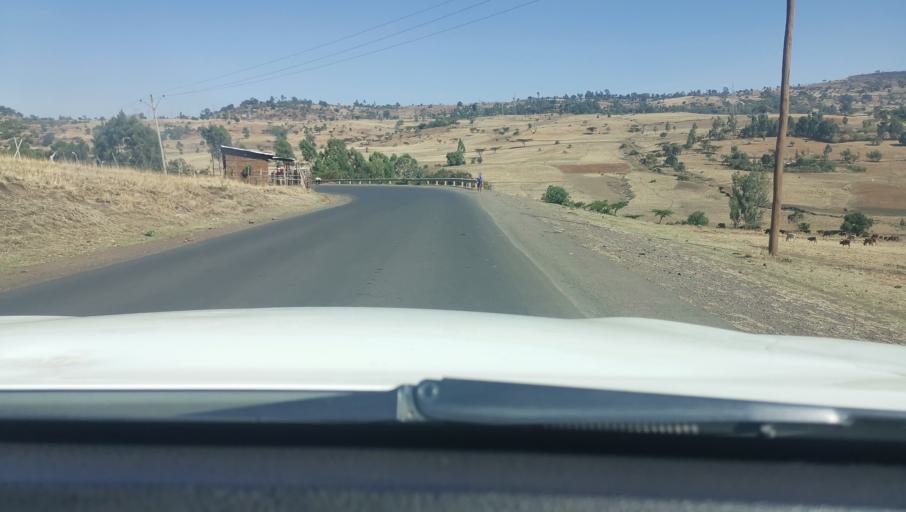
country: ET
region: Oromiya
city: Gedo
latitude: 8.9688
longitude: 37.5185
